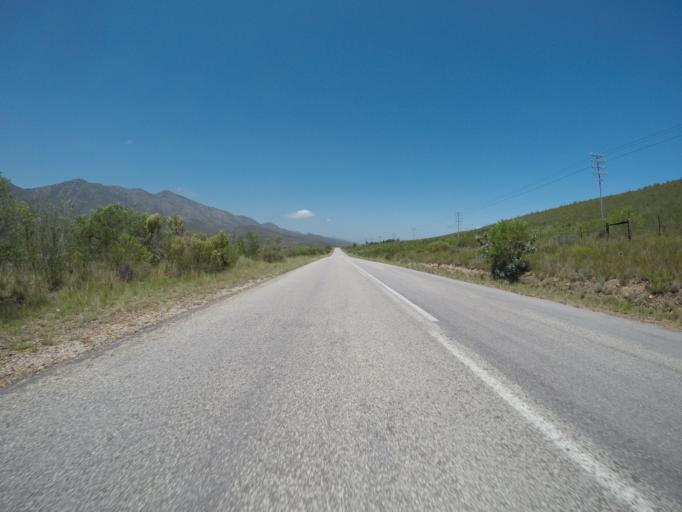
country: ZA
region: Eastern Cape
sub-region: Cacadu District Municipality
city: Kareedouw
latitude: -33.9067
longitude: 24.1513
